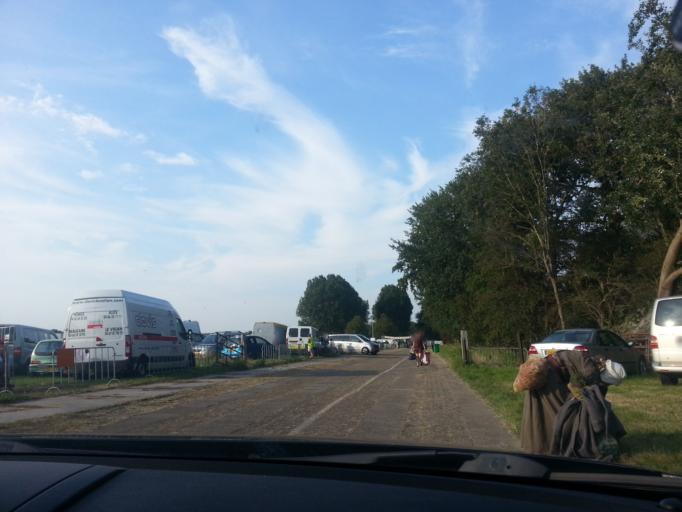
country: NL
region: South Holland
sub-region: Gemeente Lisse
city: Lisse
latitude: 52.2702
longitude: 4.5423
